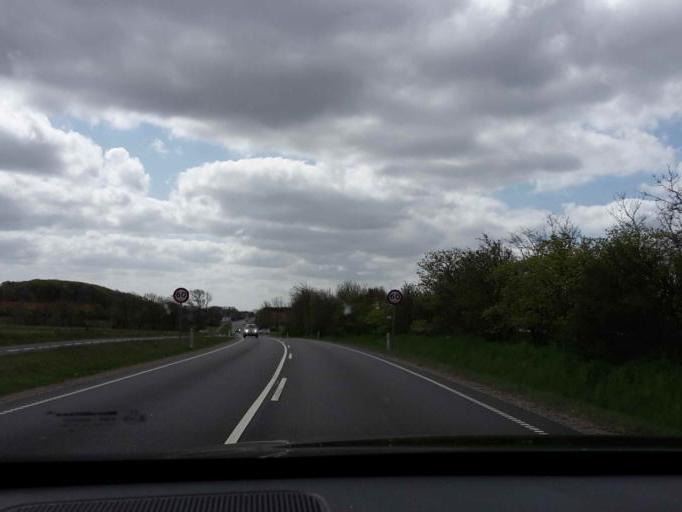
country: DK
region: South Denmark
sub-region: Varde Kommune
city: Olgod
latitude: 55.7262
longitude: 8.6130
